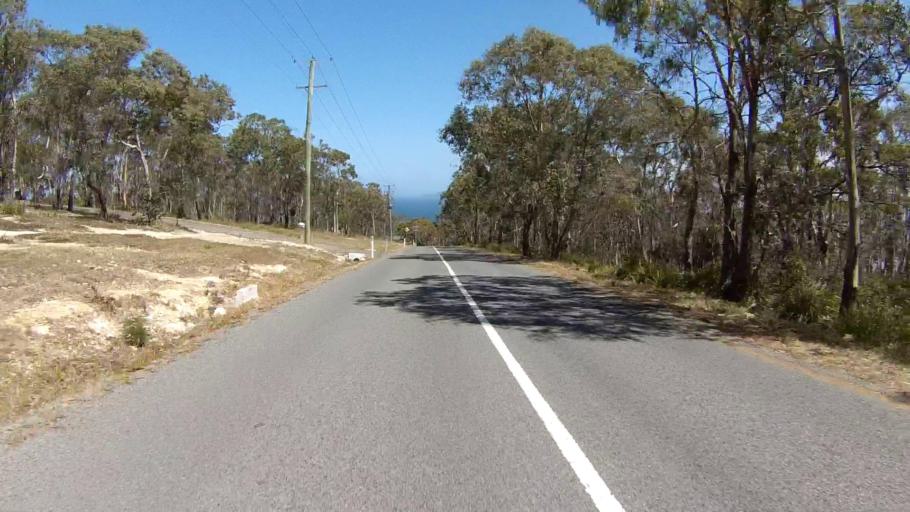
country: AU
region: Tasmania
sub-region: Clarence
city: Sandford
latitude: -43.0199
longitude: 147.4812
